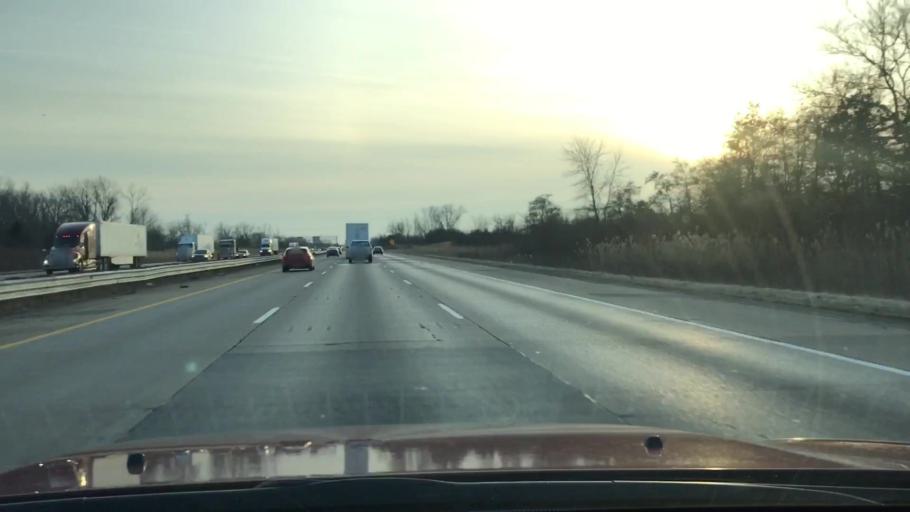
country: US
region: Michigan
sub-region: Monroe County
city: Luna Pier
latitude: 41.7901
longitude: -83.4641
